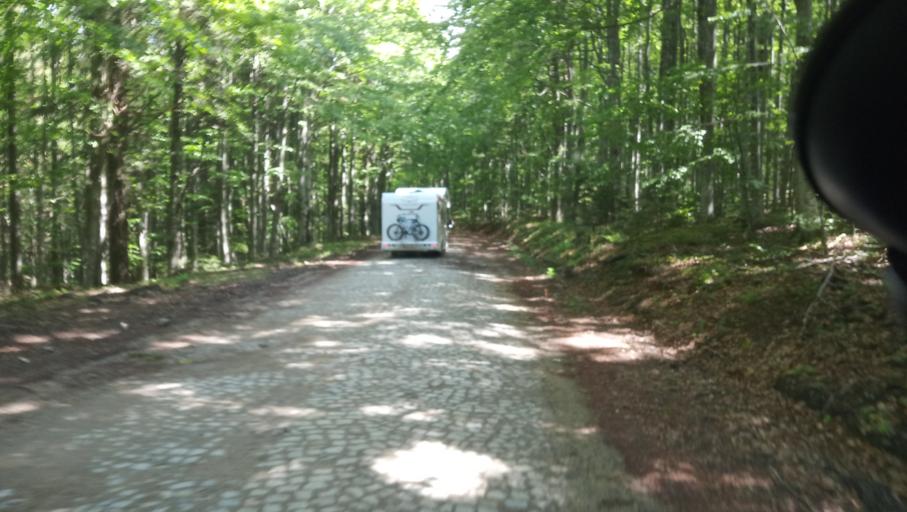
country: RO
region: Caras-Severin
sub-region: Comuna Valiug
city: Valiug
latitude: 45.2186
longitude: 22.0673
